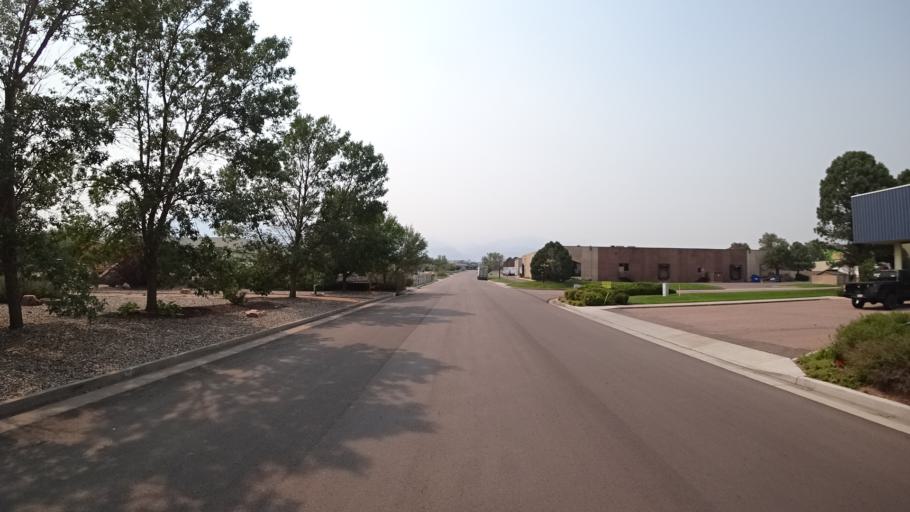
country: US
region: Colorado
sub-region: El Paso County
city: Stratmoor
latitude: 38.7919
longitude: -104.7869
